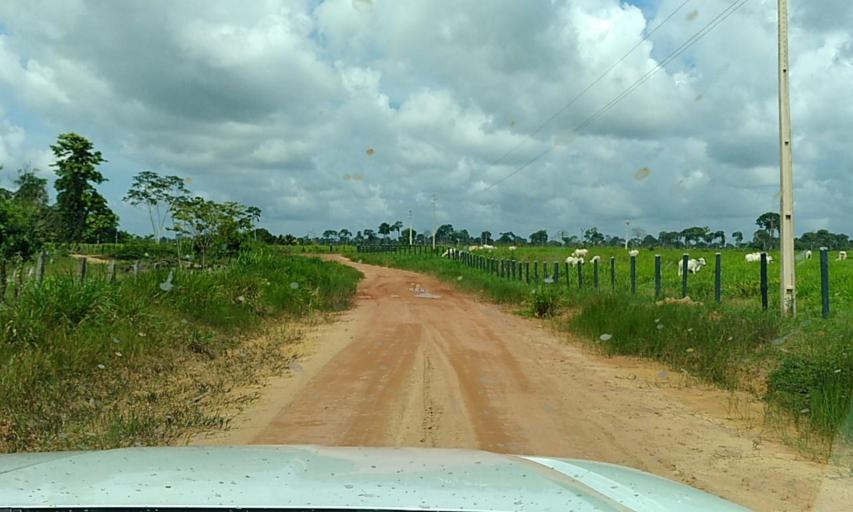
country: BR
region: Para
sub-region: Senador Jose Porfirio
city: Senador Jose Porfirio
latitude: -2.5148
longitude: -51.8426
